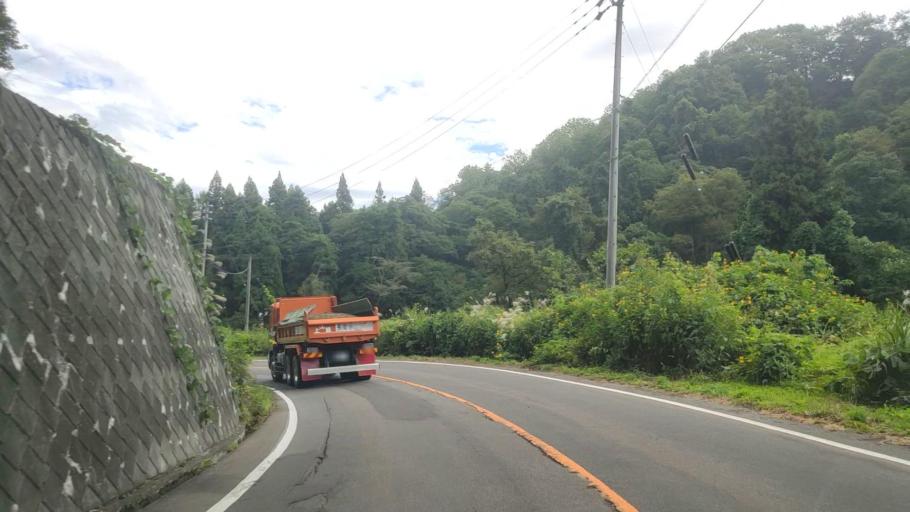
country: JP
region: Nagano
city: Iiyama
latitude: 36.8671
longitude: 138.3405
